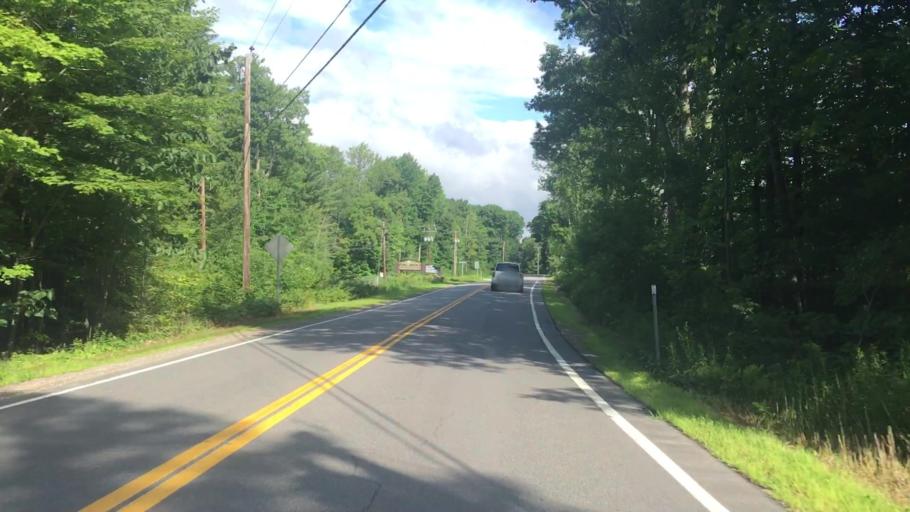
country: US
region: New Hampshire
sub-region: Belknap County
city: Gilford
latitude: 43.5495
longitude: -71.3577
